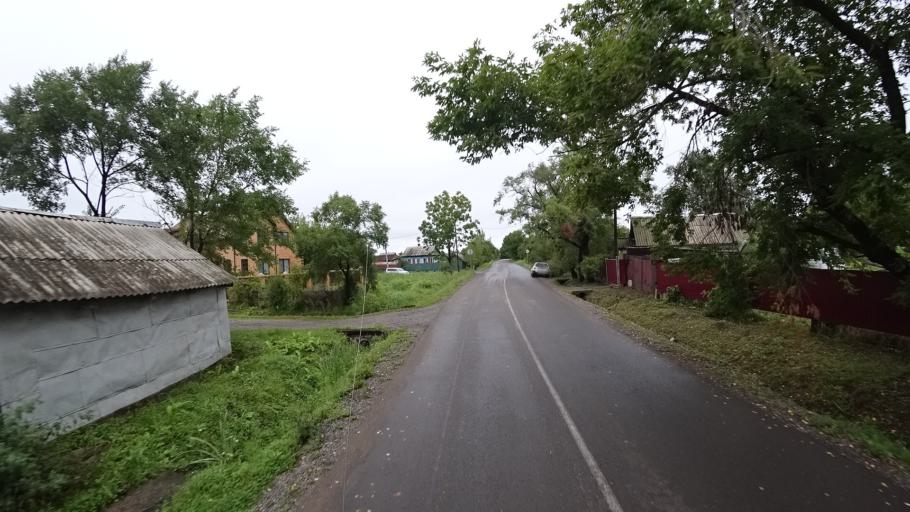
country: RU
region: Primorskiy
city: Monastyrishche
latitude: 44.2046
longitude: 132.4351
